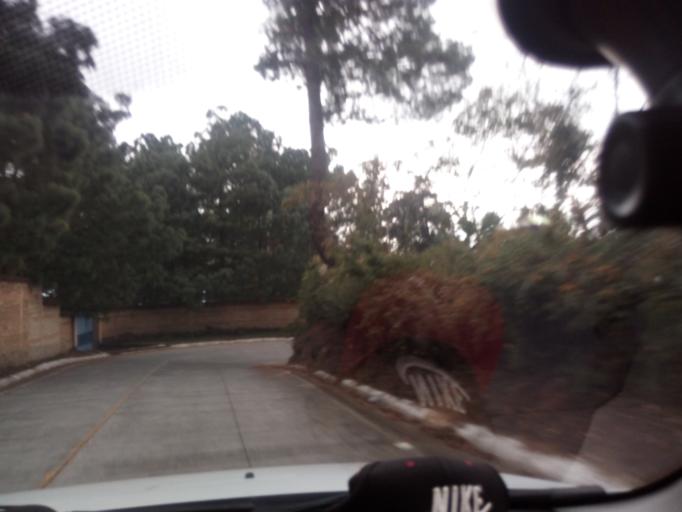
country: GT
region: Sacatepequez
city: Antigua Guatemala
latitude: 14.5696
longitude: -90.7193
